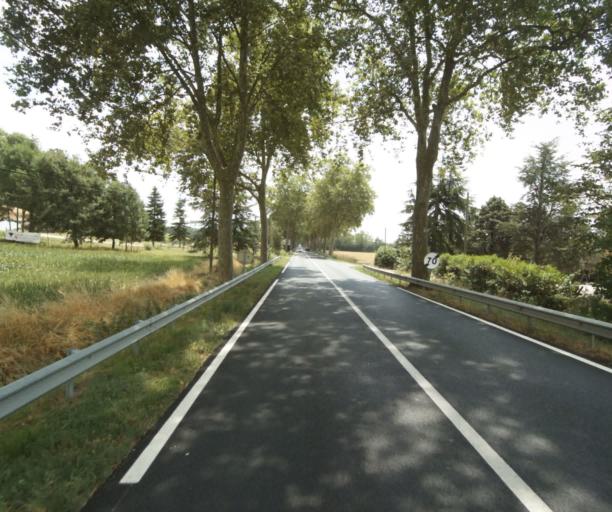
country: FR
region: Midi-Pyrenees
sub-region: Departement de la Haute-Garonne
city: Revel
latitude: 43.4440
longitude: 1.9516
